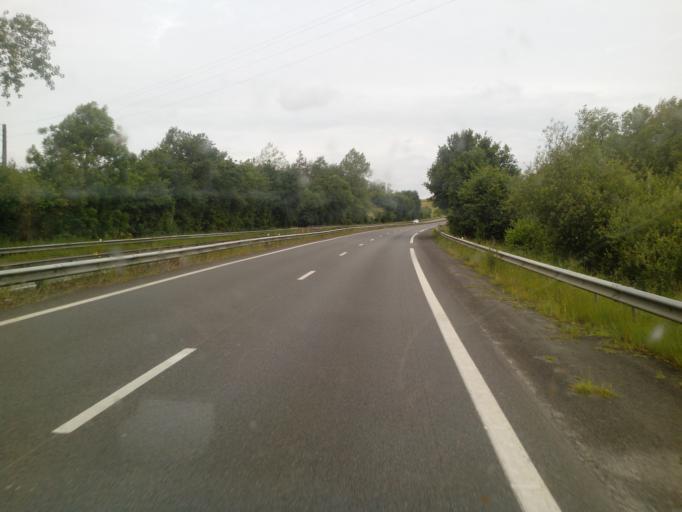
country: FR
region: Brittany
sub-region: Departement des Cotes-d'Armor
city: Broons
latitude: 48.2992
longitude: -2.2312
